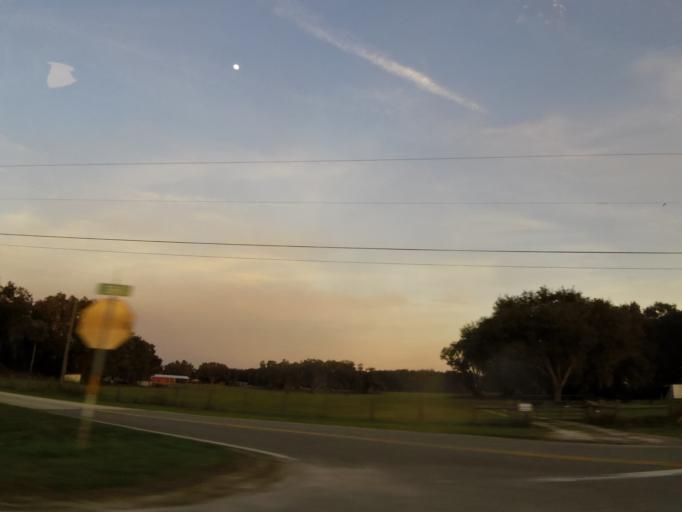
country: US
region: Florida
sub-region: Volusia County
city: De Leon Springs
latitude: 29.1201
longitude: -81.2859
